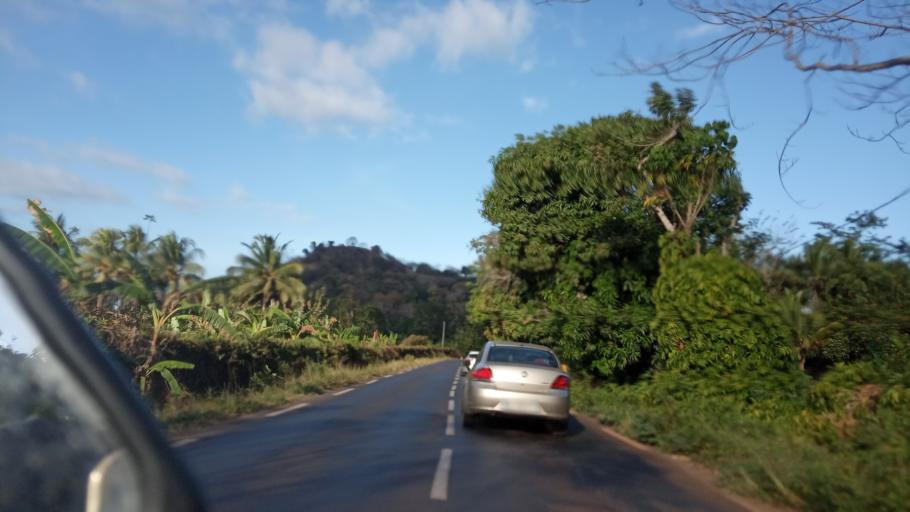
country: YT
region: Dembeni
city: Dembeni
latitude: -12.8686
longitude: 45.2013
